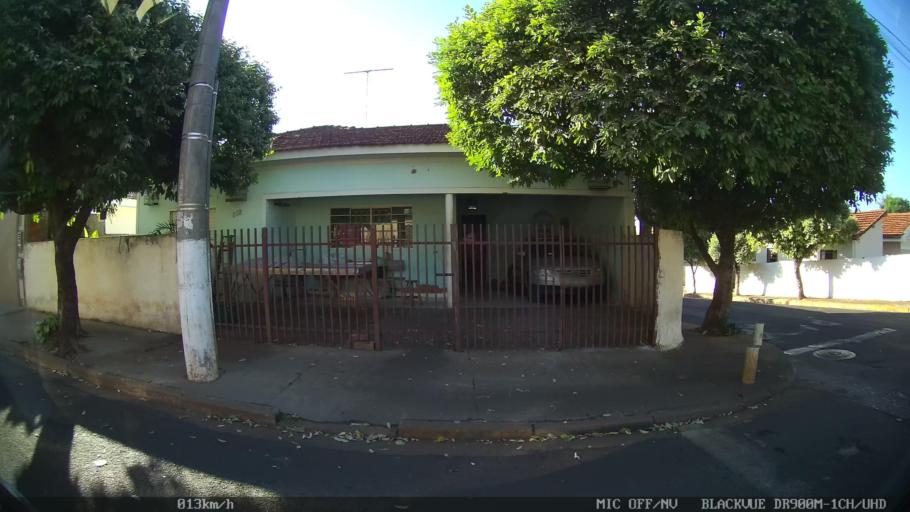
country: BR
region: Sao Paulo
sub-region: Guapiacu
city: Guapiacu
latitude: -20.7942
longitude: -49.2237
